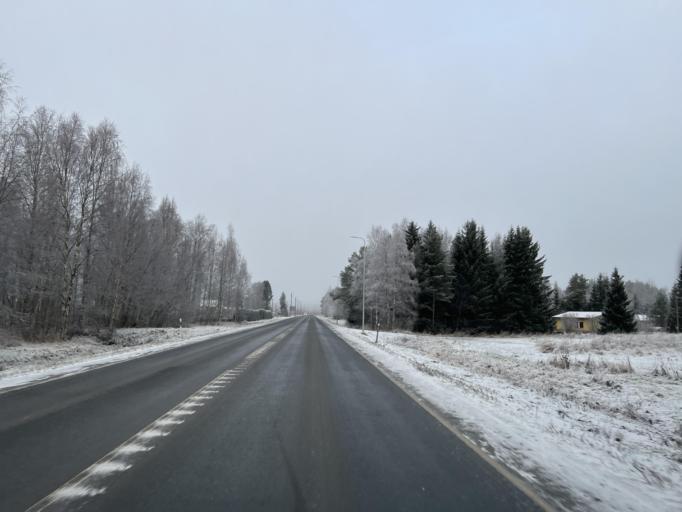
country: FI
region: Northern Ostrobothnia
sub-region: Oulunkaari
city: Utajaervi
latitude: 64.7452
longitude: 26.4409
